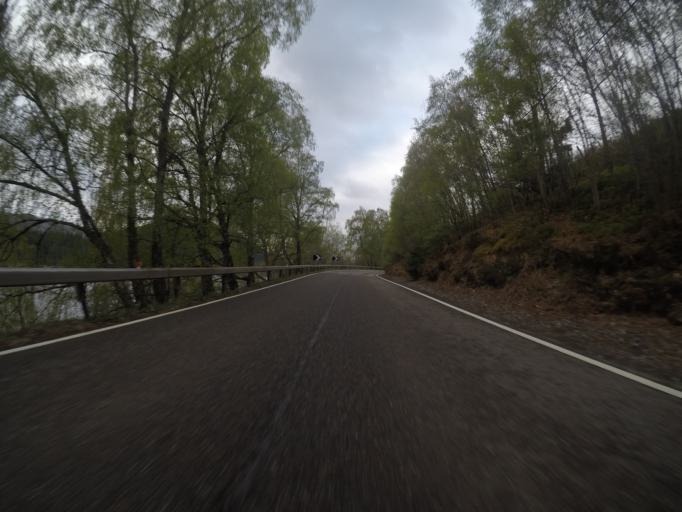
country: GB
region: Scotland
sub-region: Highland
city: Kingussie
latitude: 56.9593
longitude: -4.4631
